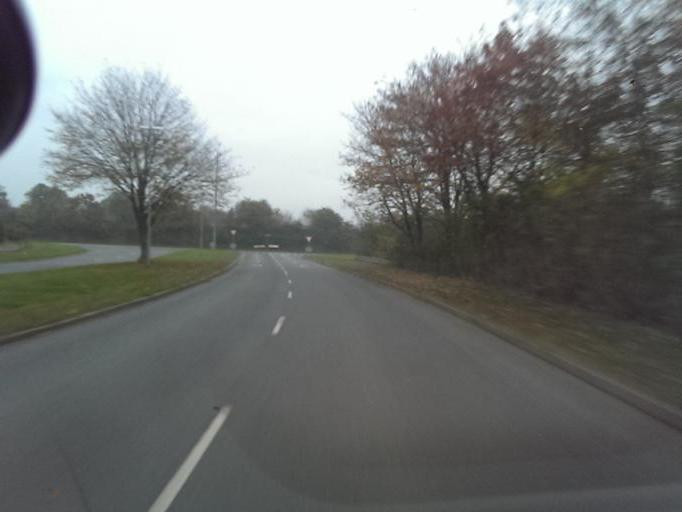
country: DK
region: South Denmark
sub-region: Esbjerg Kommune
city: Esbjerg
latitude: 55.5070
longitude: 8.4316
